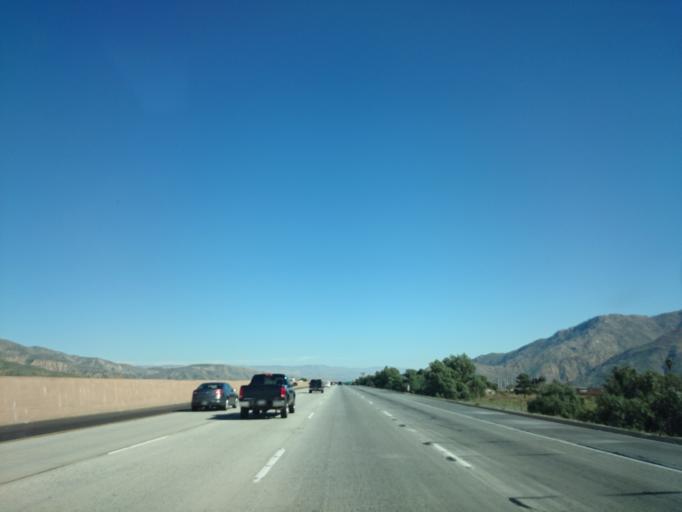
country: US
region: California
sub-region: Riverside County
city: Cabazon
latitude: 33.9186
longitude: -116.7892
